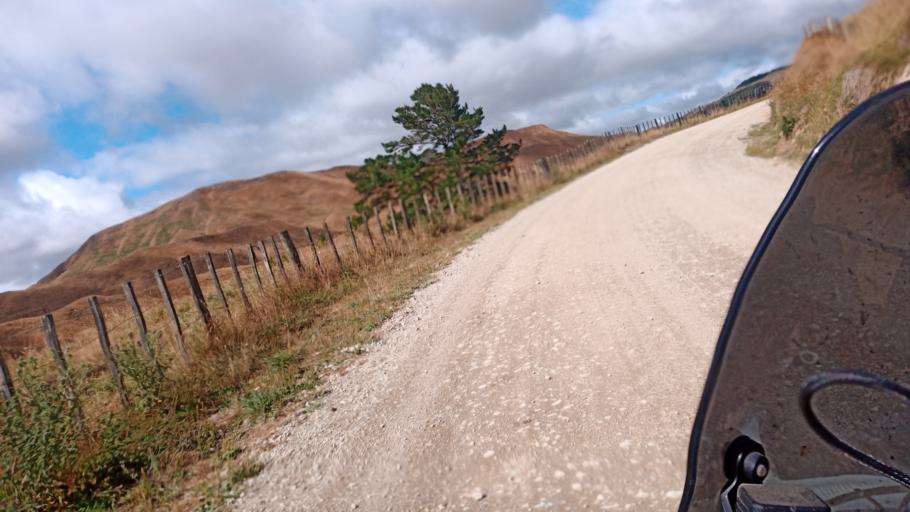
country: NZ
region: Hawke's Bay
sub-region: Wairoa District
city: Wairoa
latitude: -38.6072
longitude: 177.4517
